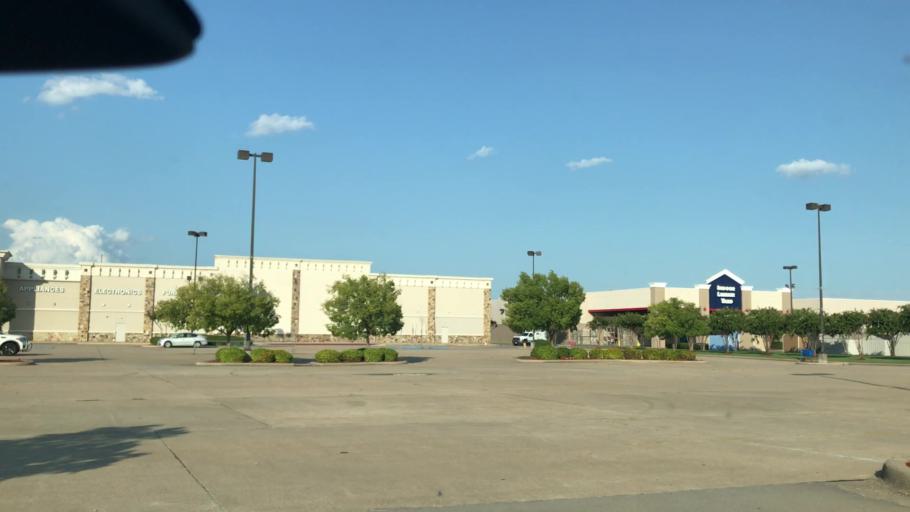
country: US
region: Louisiana
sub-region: Bossier Parish
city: Bossier City
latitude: 32.4415
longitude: -93.7163
